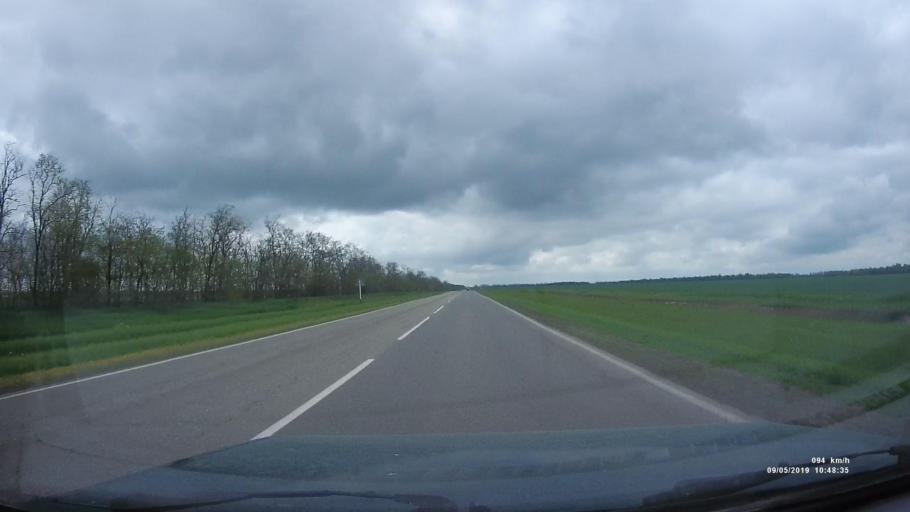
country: RU
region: Rostov
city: Peshkovo
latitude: 46.9545
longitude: 39.3554
